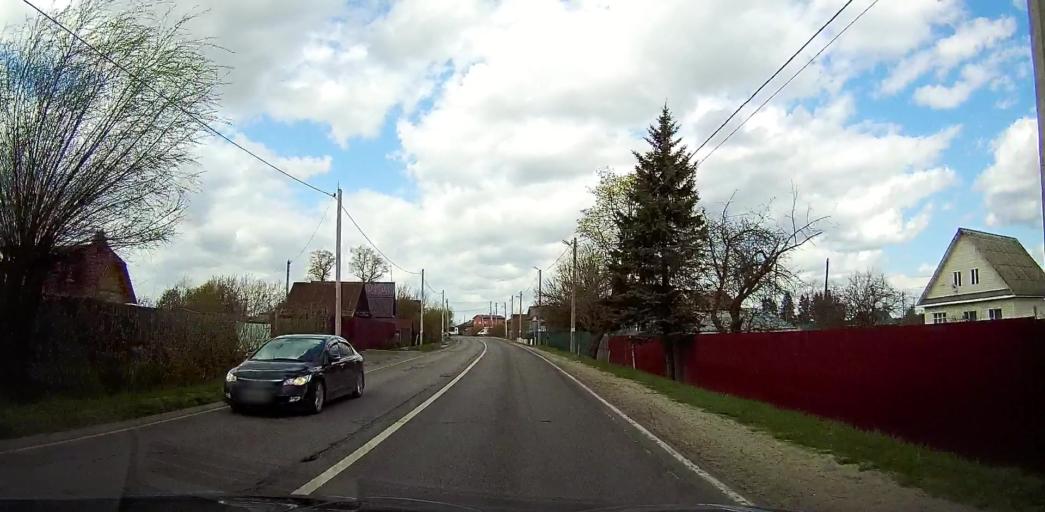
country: RU
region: Moskovskaya
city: Davydovo
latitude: 55.6352
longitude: 38.8691
